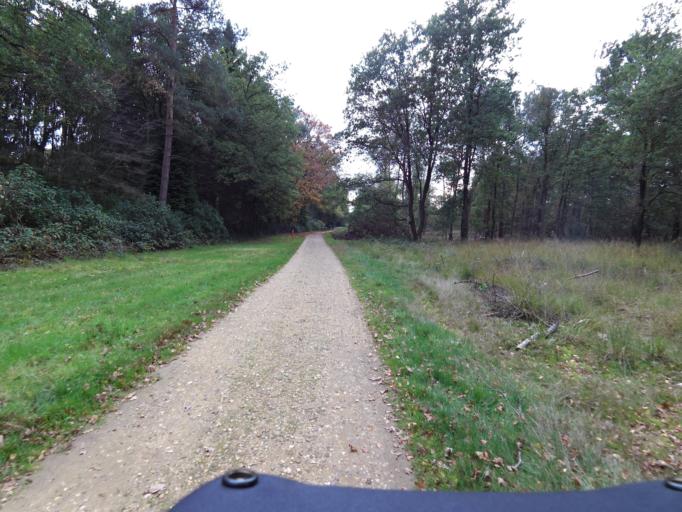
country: BE
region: Flanders
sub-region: Provincie Antwerpen
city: Kalmthout
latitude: 51.3861
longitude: 4.4493
